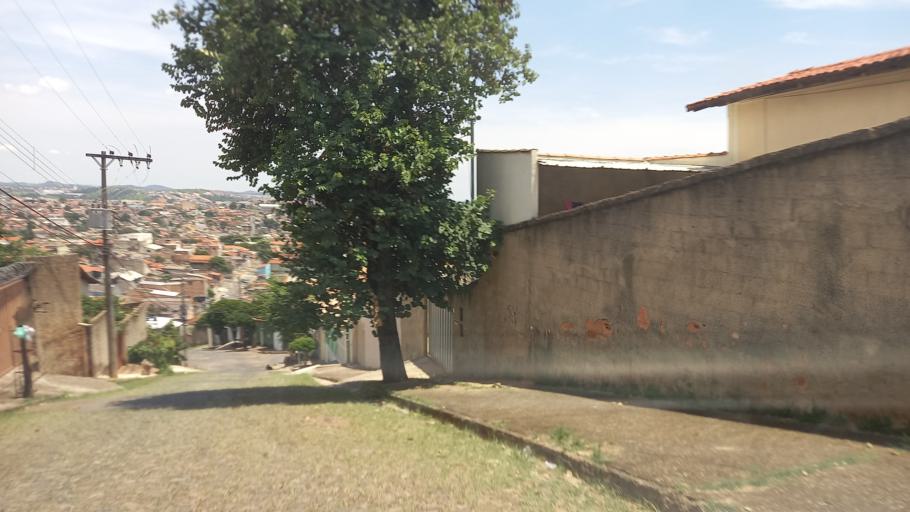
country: BR
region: Minas Gerais
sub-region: Contagem
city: Contagem
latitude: -19.9058
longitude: -44.0123
